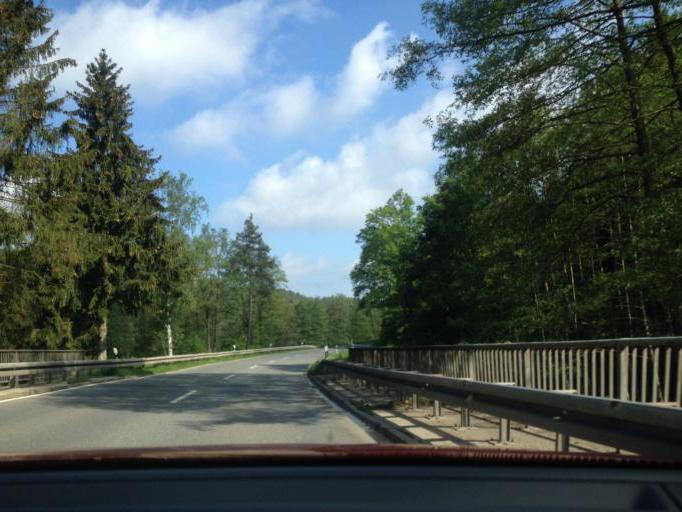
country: DE
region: Bavaria
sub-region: Upper Palatinate
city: Neusorg
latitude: 49.9159
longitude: 11.9681
